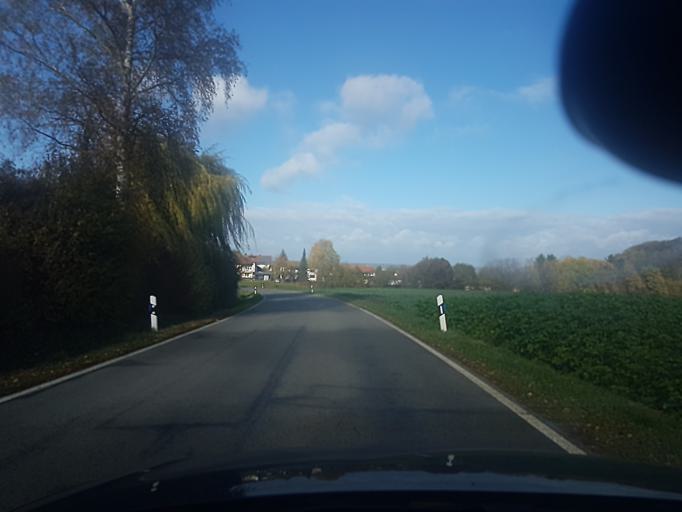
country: DE
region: Bavaria
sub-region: Lower Bavaria
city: Loiching
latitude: 48.6161
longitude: 12.4577
